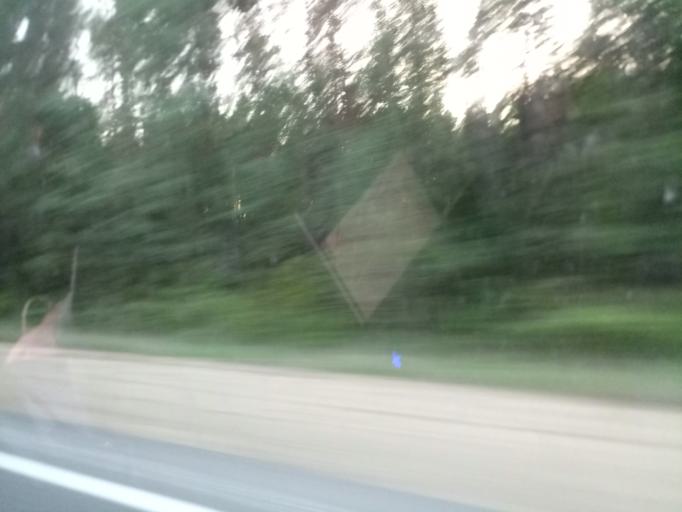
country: RU
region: Moskovskaya
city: Noginsk-9
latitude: 56.0773
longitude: 38.5721
